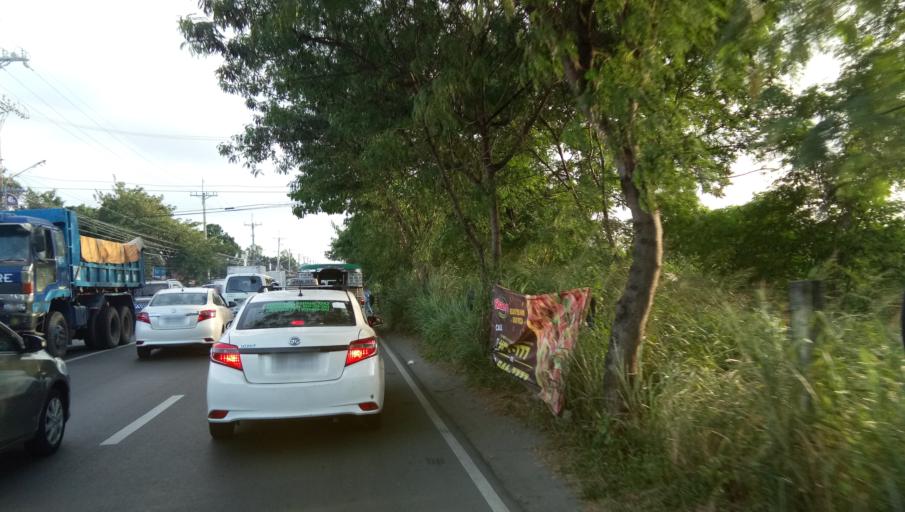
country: PH
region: Calabarzon
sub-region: Province of Cavite
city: Dasmarinas
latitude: 14.3751
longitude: 120.9796
